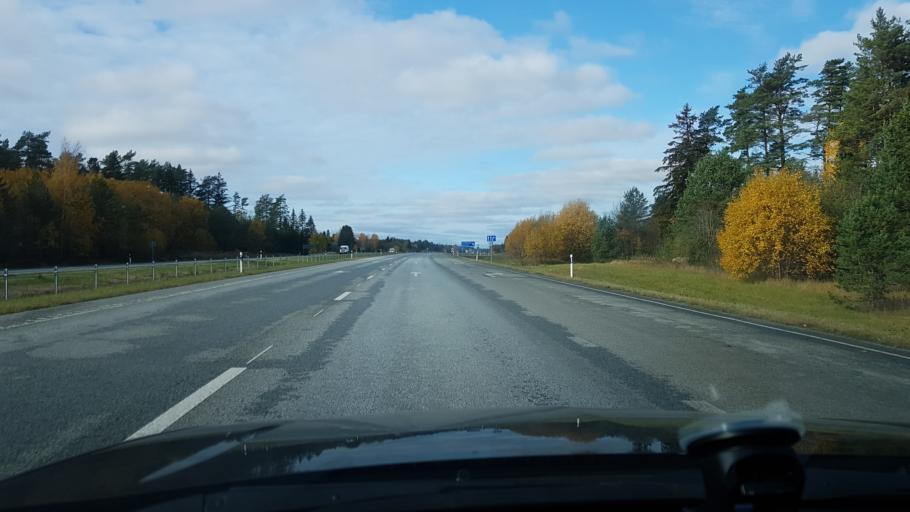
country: EE
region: Laeaene-Virumaa
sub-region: Kadrina vald
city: Kadrina
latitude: 59.4478
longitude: 26.0778
